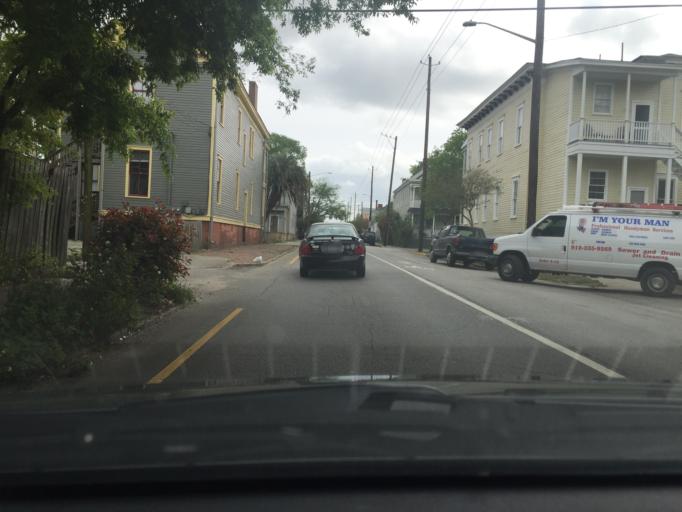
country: US
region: Georgia
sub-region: Chatham County
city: Savannah
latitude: 32.0639
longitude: -81.0918
